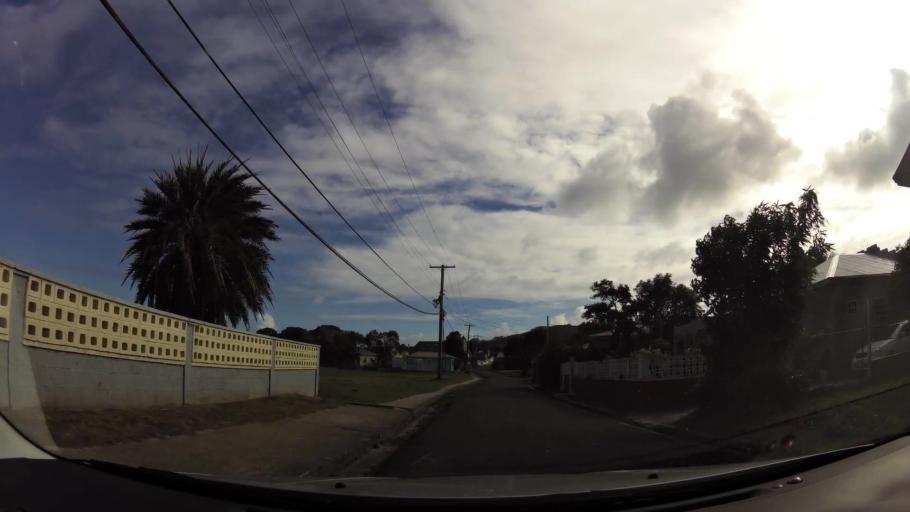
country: AG
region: Saint Peter
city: All Saints
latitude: 17.0512
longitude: -61.8012
